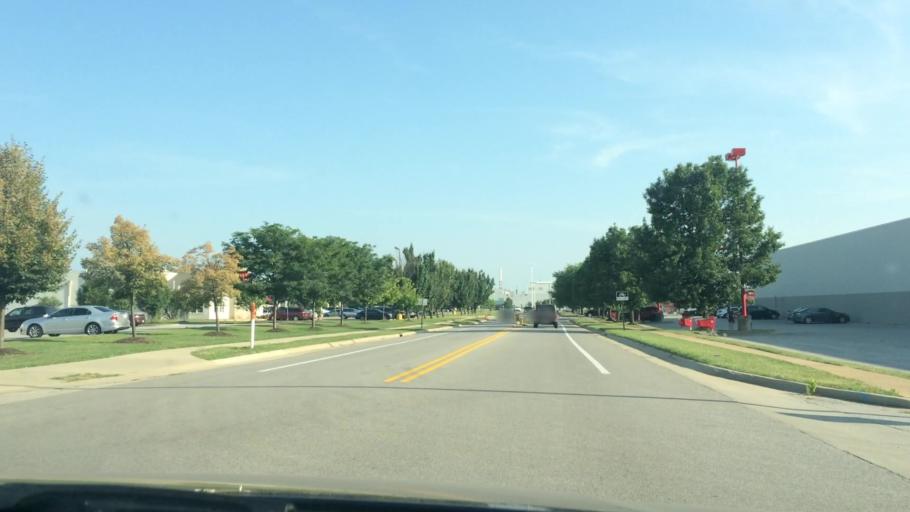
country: US
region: Indiana
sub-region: Tippecanoe County
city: Lafayette
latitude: 40.4206
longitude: -86.8461
